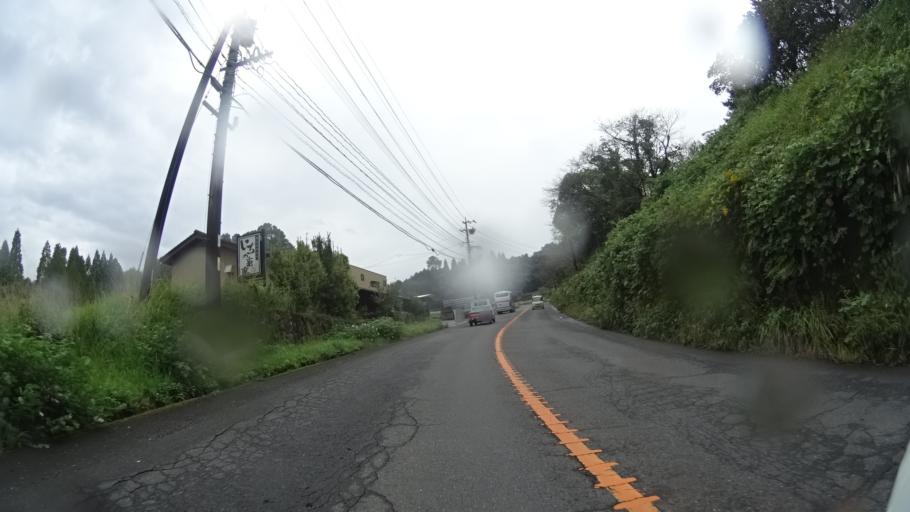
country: JP
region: Kagoshima
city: Kajiki
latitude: 31.7703
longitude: 130.6704
